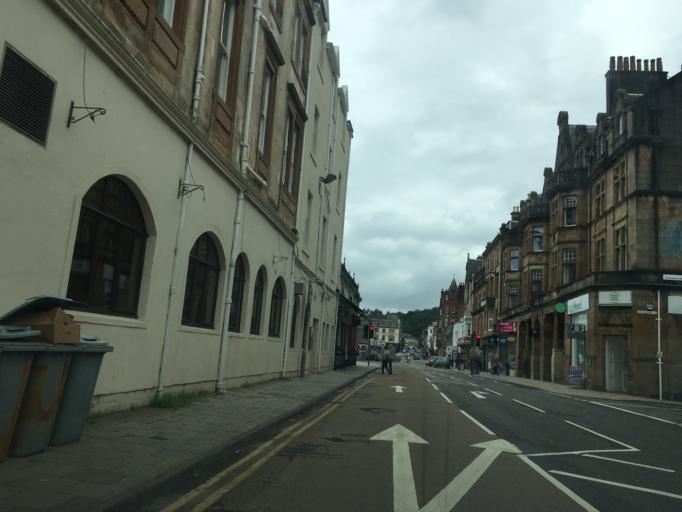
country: GB
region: Scotland
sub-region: Argyll and Bute
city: Oban
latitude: 56.4129
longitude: -5.4722
